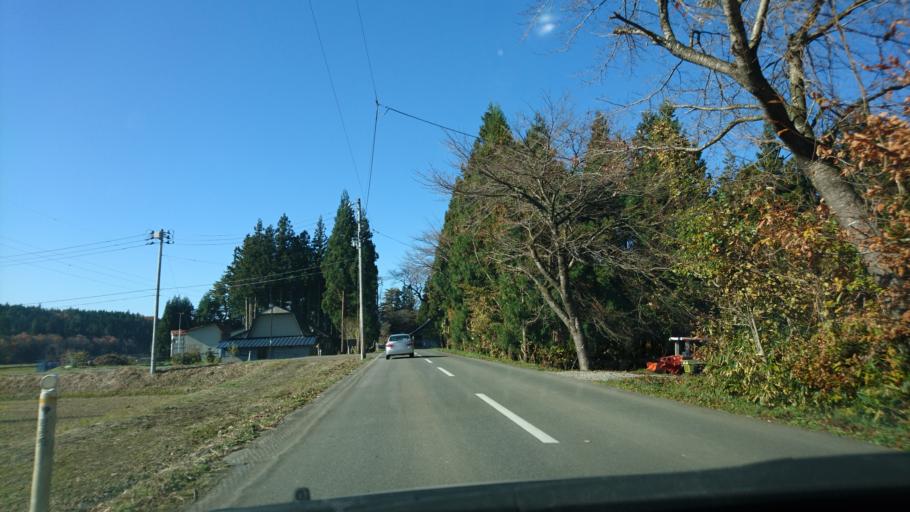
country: JP
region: Iwate
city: Mizusawa
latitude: 39.1236
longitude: 140.9745
